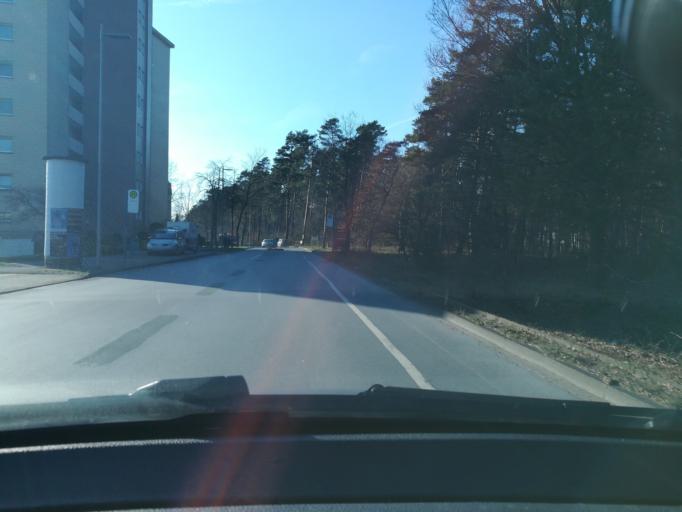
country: DE
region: North Rhine-Westphalia
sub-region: Regierungsbezirk Detmold
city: Oerlinghausen
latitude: 51.9564
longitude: 8.6001
